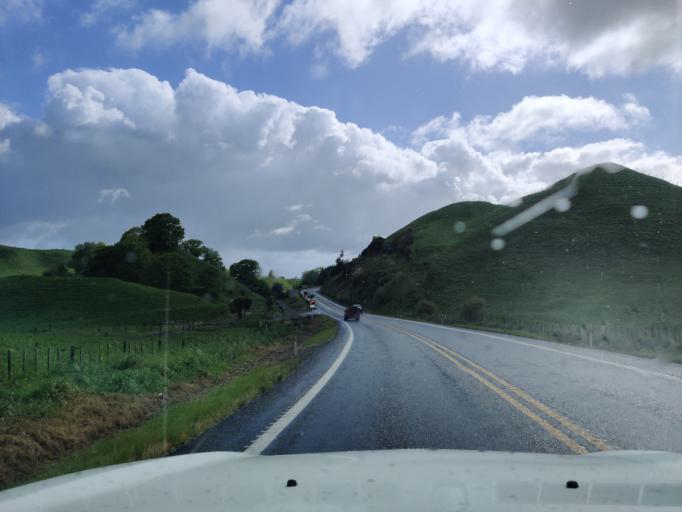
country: NZ
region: Waikato
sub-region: Matamata-Piako District
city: Matamata
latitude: -37.9770
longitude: 175.7415
